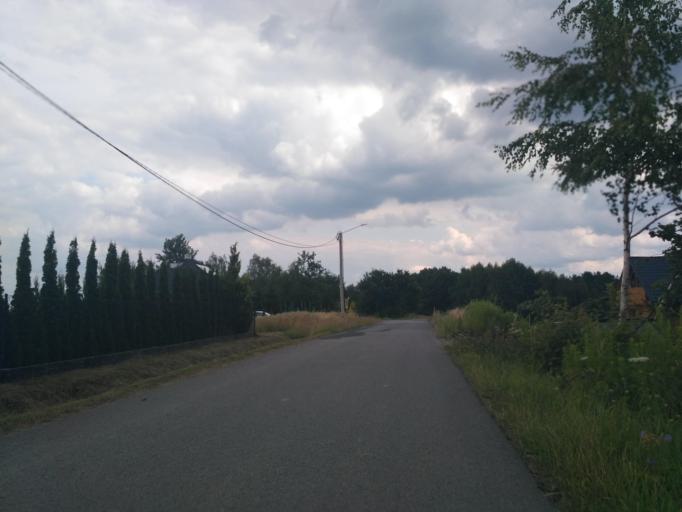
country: PL
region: Subcarpathian Voivodeship
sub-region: Powiat ropczycko-sedziszowski
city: Niedzwiada
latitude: 50.0282
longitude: 21.5242
